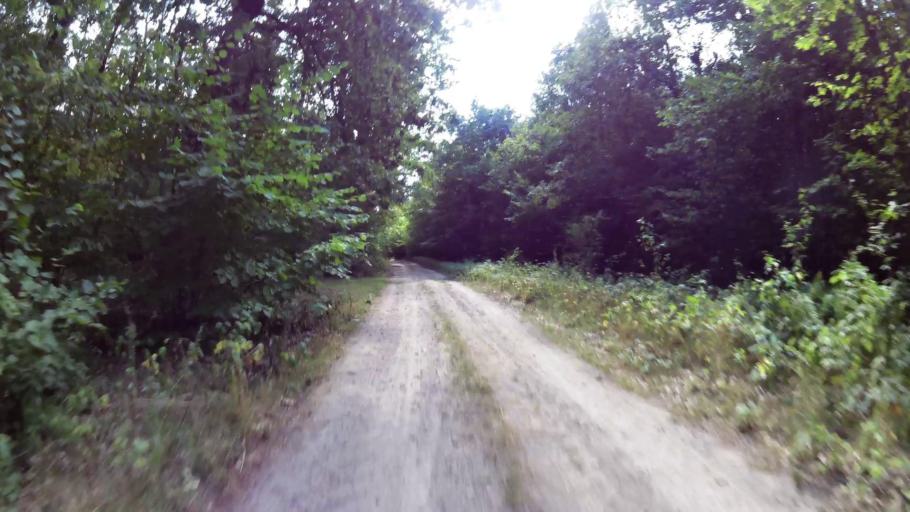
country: PL
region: West Pomeranian Voivodeship
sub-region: Powiat gryfinski
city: Moryn
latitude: 52.8798
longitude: 14.4300
